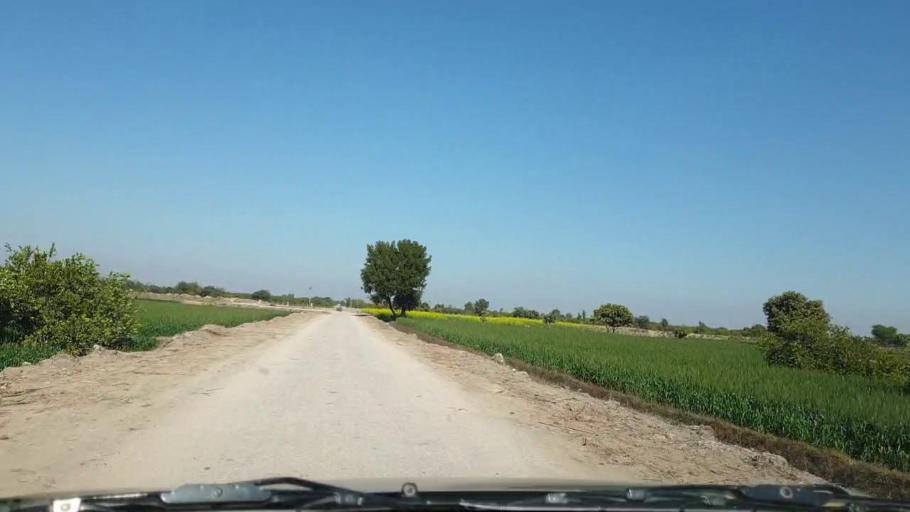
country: PK
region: Sindh
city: Sinjhoro
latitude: 26.1299
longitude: 68.8162
